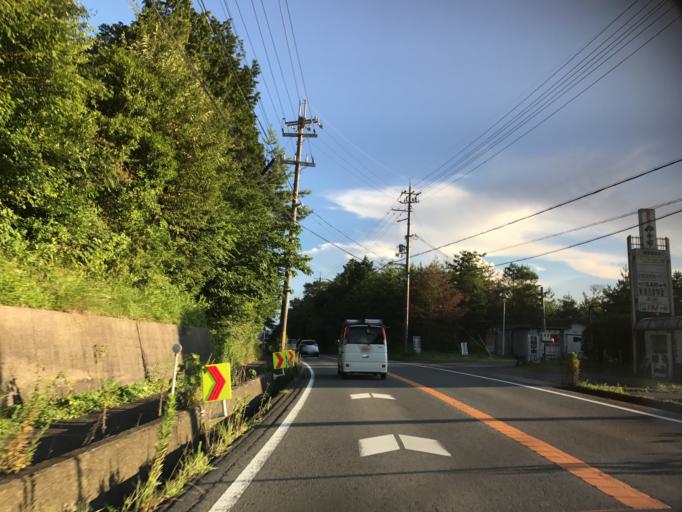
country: JP
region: Shiga Prefecture
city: Hino
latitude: 35.0282
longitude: 136.2399
